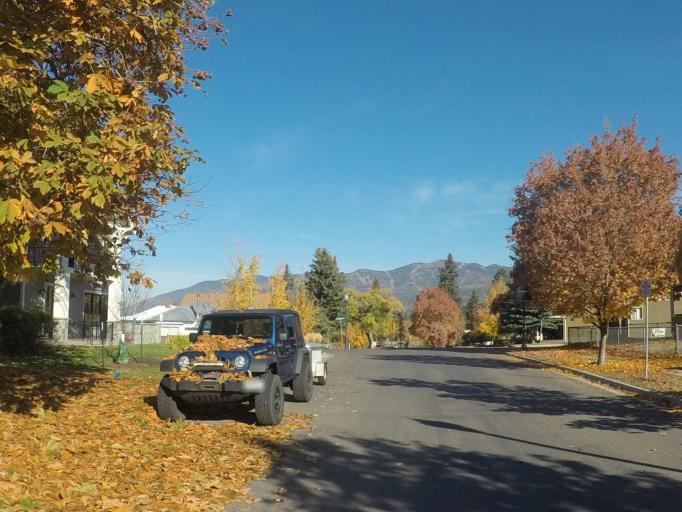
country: US
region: Montana
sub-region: Flathead County
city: Whitefish
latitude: 48.4156
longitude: -114.3507
